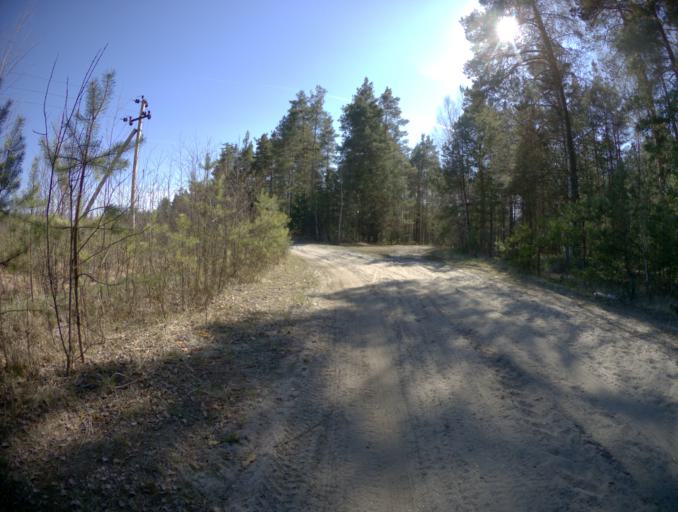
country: RU
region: Vladimir
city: Ivanishchi
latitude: 55.7633
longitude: 40.4073
